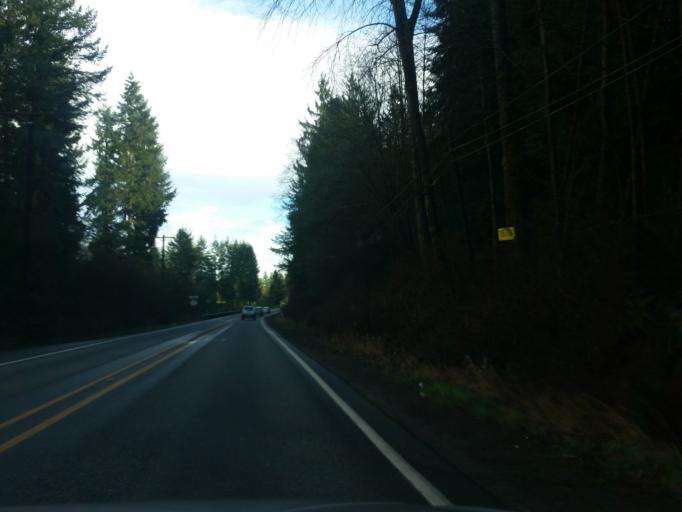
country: US
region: Washington
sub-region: Snohomish County
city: Martha Lake
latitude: 47.8259
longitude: -122.2470
